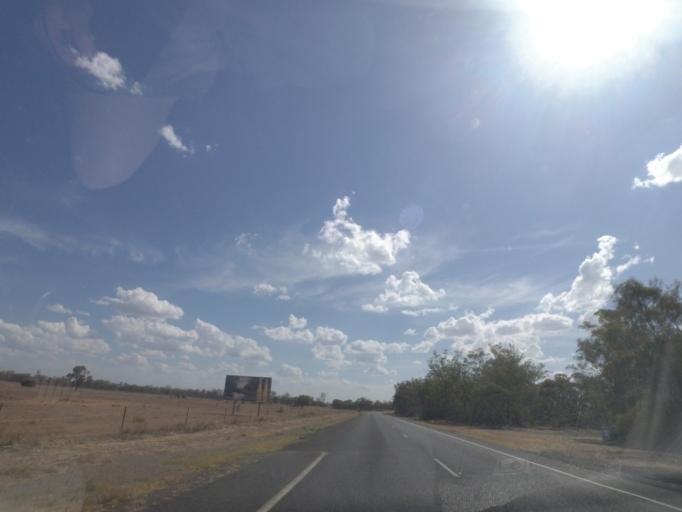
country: AU
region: Queensland
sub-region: Southern Downs
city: Stanthorpe
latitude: -28.4116
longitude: 151.1676
